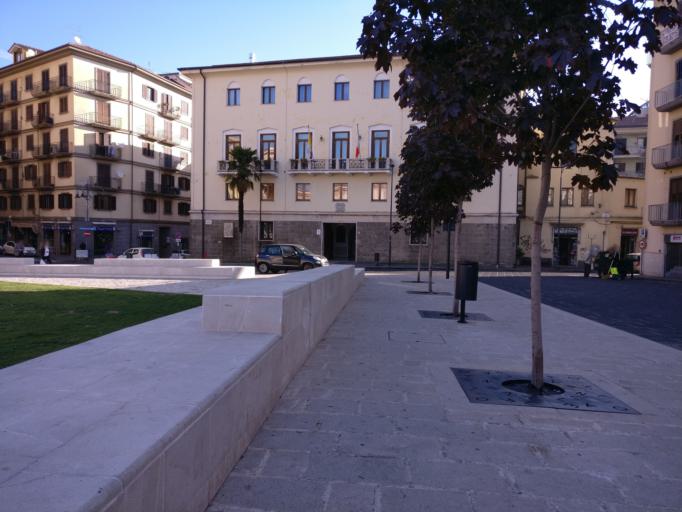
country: IT
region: Campania
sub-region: Provincia di Avellino
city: Avellino
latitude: 40.9145
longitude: 14.7929
